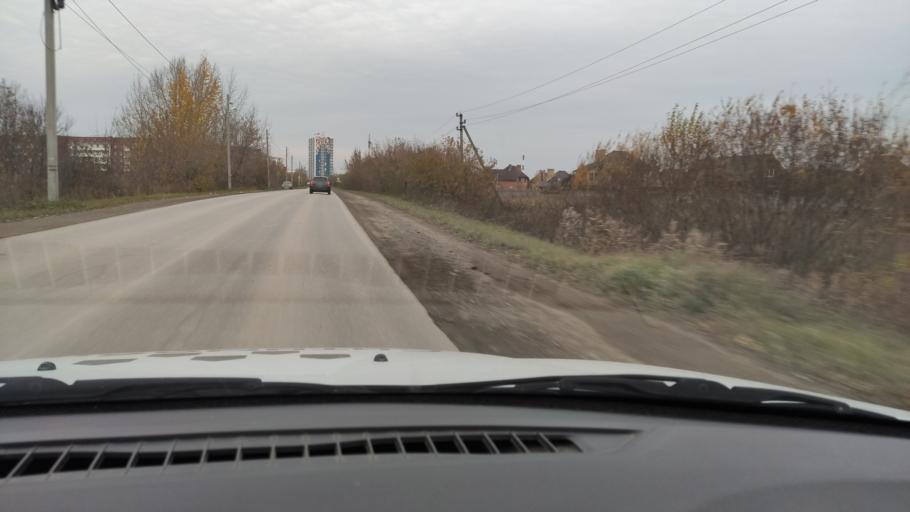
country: RU
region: Perm
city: Kondratovo
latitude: 57.9709
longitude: 56.1138
